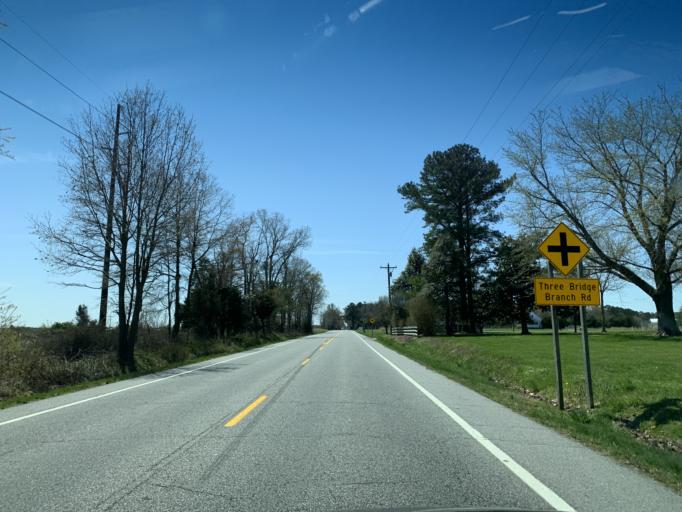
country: US
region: Maryland
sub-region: Talbot County
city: Easton
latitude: 38.8548
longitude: -76.0133
